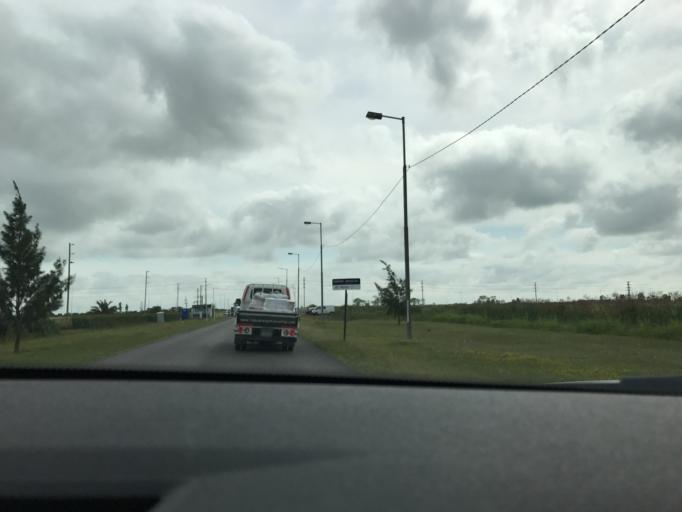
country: AR
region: Buenos Aires
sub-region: Partido de La Plata
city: La Plata
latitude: -34.8427
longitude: -58.0736
